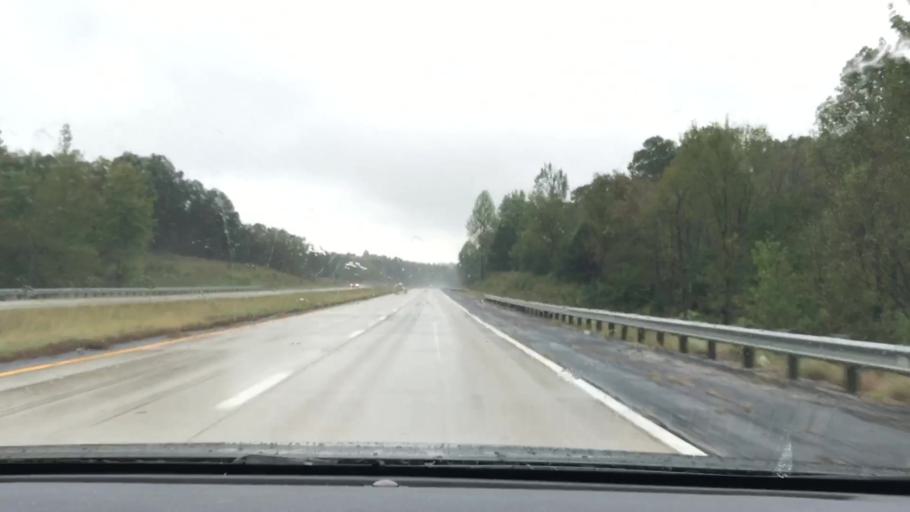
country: US
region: Kentucky
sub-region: Hopkins County
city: Nortonville
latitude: 37.1377
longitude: -87.4605
